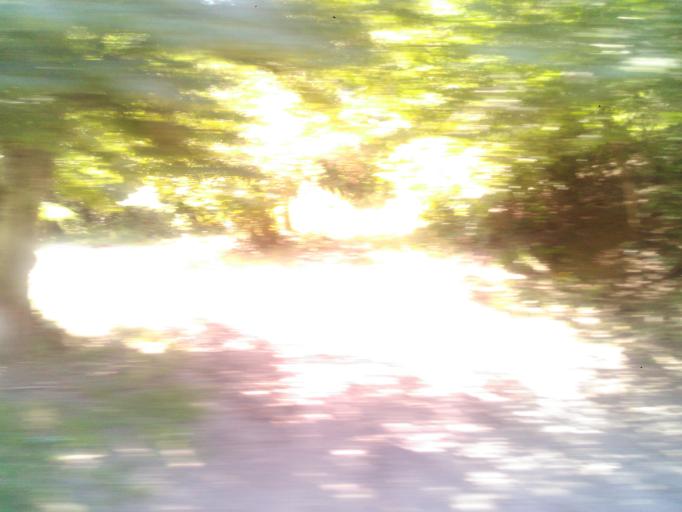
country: GE
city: Zhinvali
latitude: 42.1879
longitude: 44.8196
